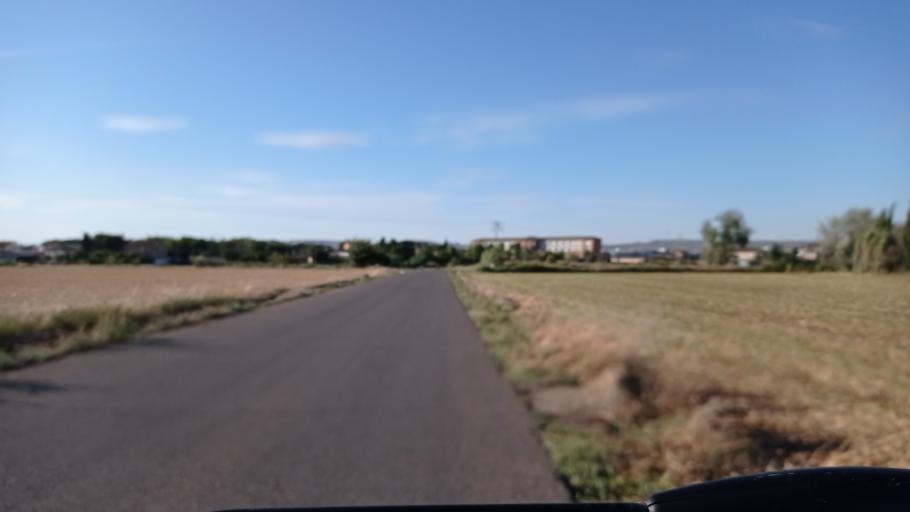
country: ES
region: Aragon
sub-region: Provincia de Zaragoza
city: Oliver-Valdefierro, Oliver, Valdefierro
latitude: 41.6738
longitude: -0.9666
